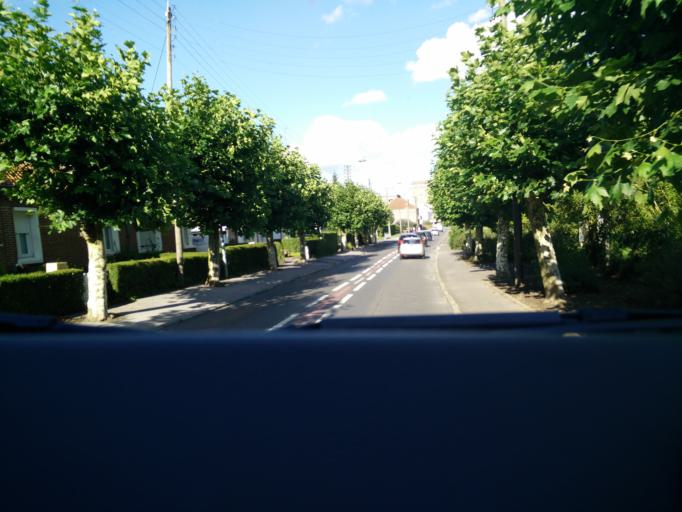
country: FR
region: Nord-Pas-de-Calais
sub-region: Departement du Nord
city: Maubeuge
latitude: 50.2839
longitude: 3.9773
